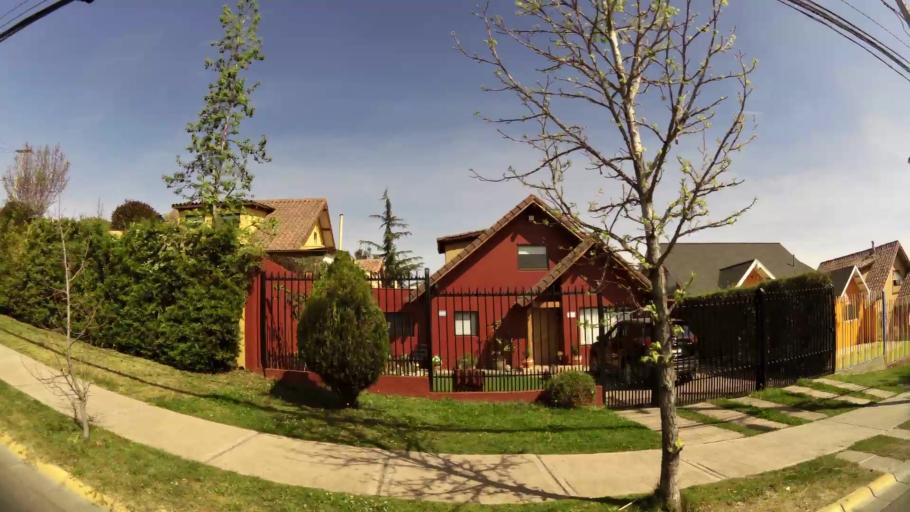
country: CL
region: Santiago Metropolitan
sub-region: Provincia de Cordillera
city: Puente Alto
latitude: -33.5357
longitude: -70.5501
